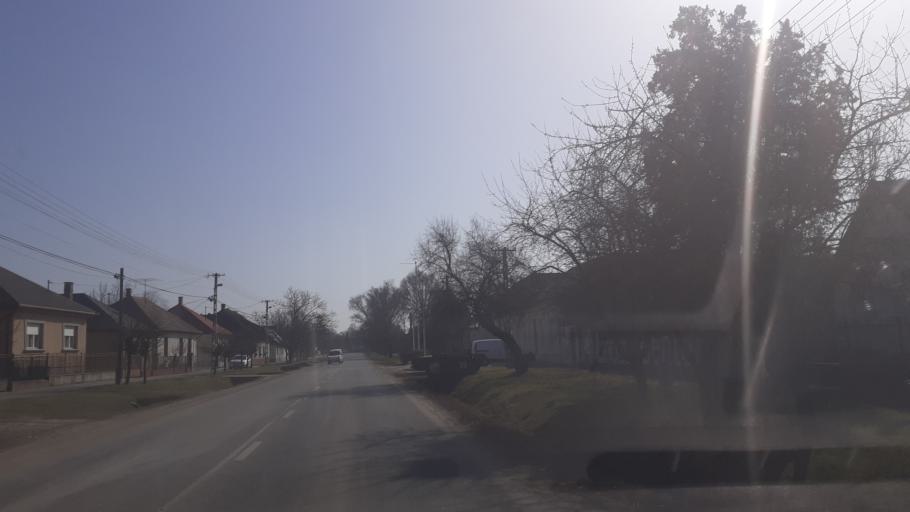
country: HU
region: Pest
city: Dabas
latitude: 47.1698
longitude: 19.3244
